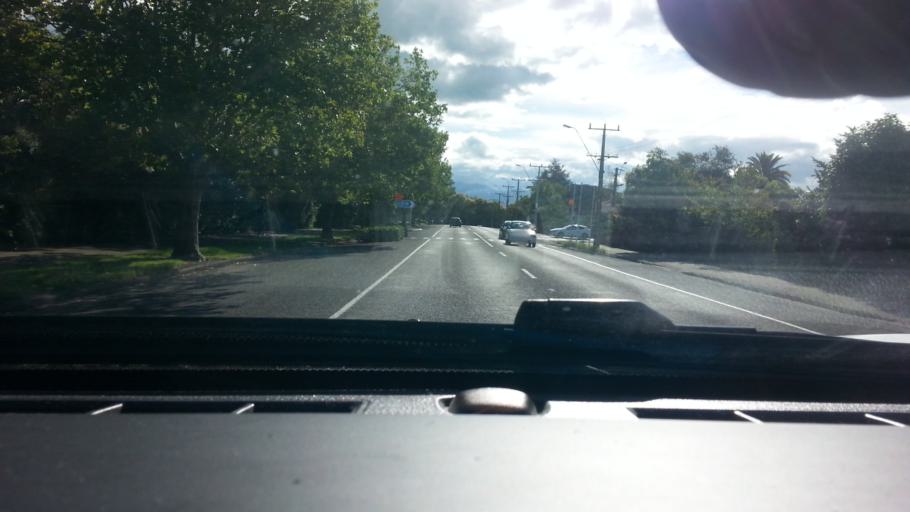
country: NZ
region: Wellington
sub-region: Masterton District
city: Masterton
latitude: -40.9458
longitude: 175.6723
